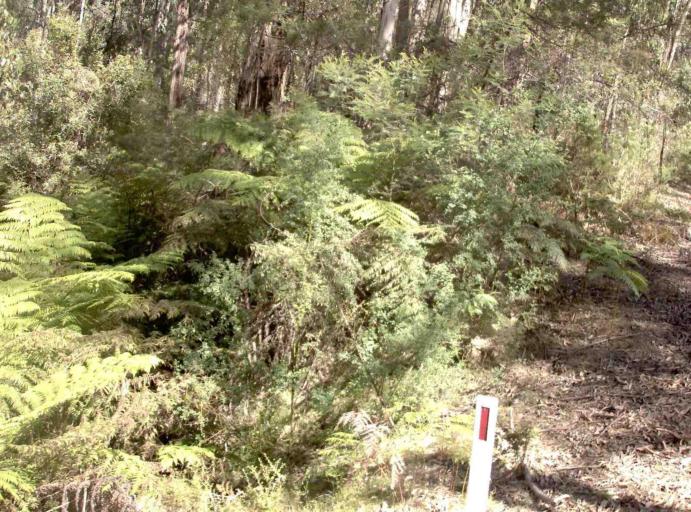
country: AU
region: New South Wales
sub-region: Bombala
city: Bombala
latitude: -37.2880
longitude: 148.7151
